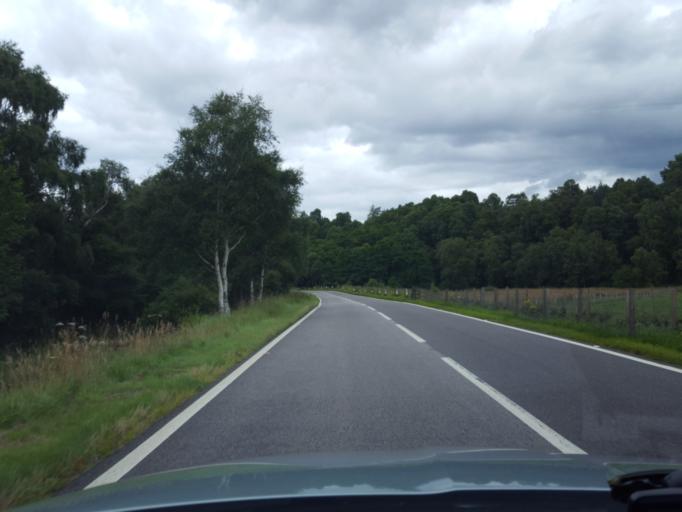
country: GB
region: Scotland
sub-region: Highland
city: Grantown on Spey
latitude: 57.3780
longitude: -3.4655
